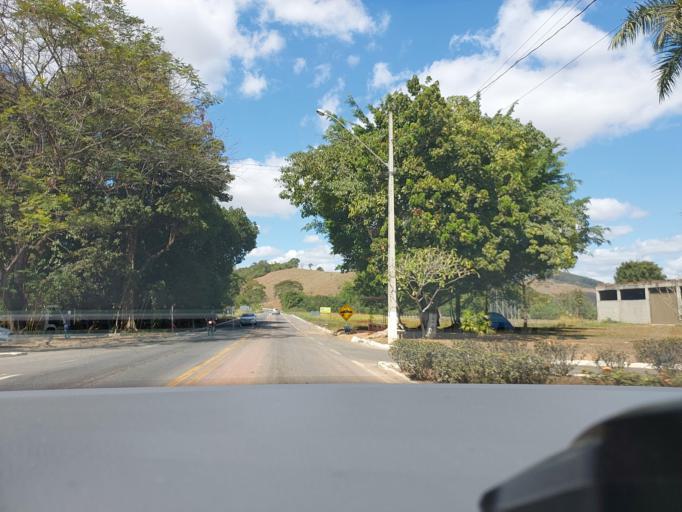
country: BR
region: Minas Gerais
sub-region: Muriae
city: Muriae
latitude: -21.1281
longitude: -42.2004
